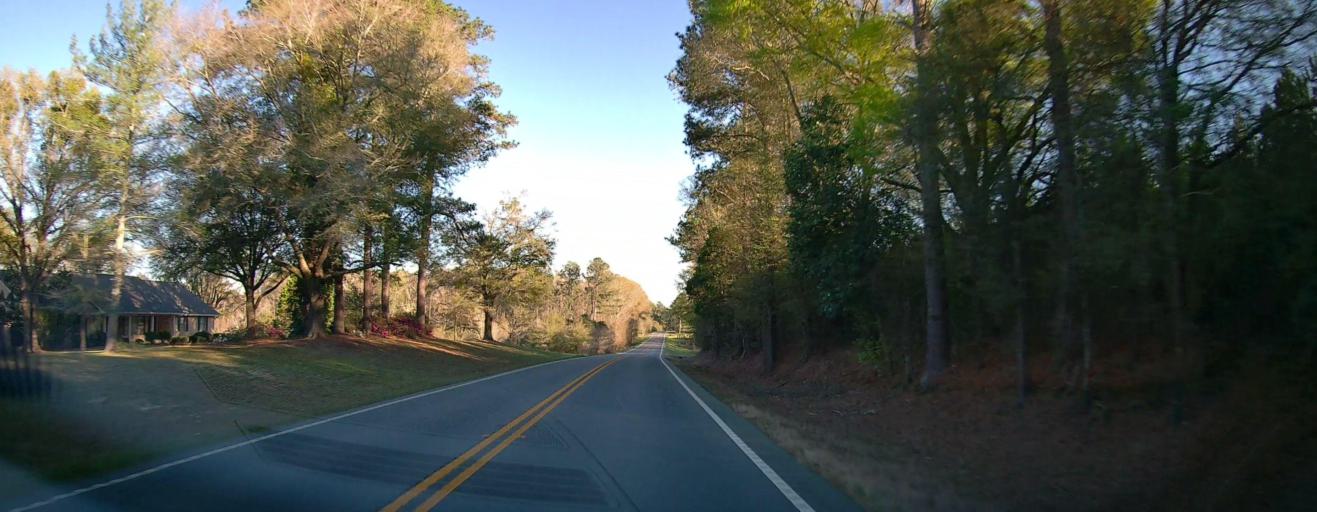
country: US
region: Georgia
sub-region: Pulaski County
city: Hawkinsville
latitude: 32.2397
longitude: -83.4032
